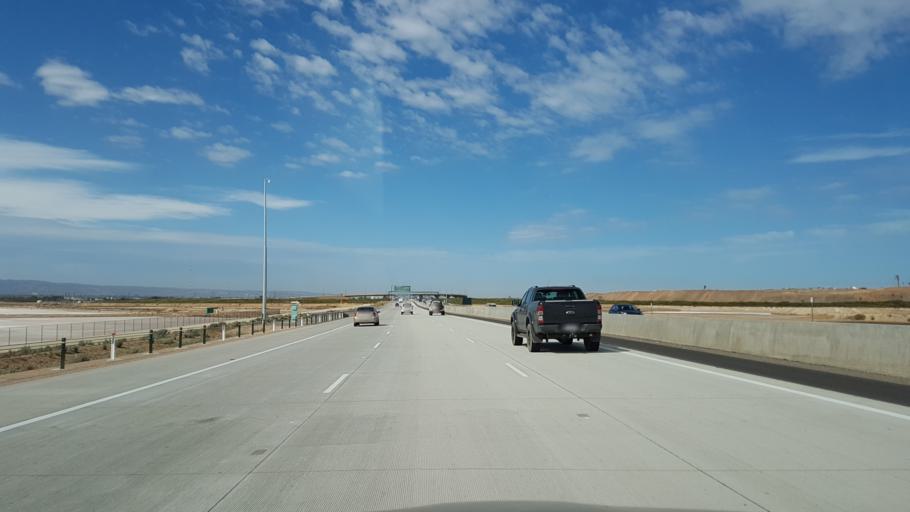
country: AU
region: South Australia
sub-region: Port Adelaide Enfield
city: Enfield
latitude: -34.8183
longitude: 138.5618
